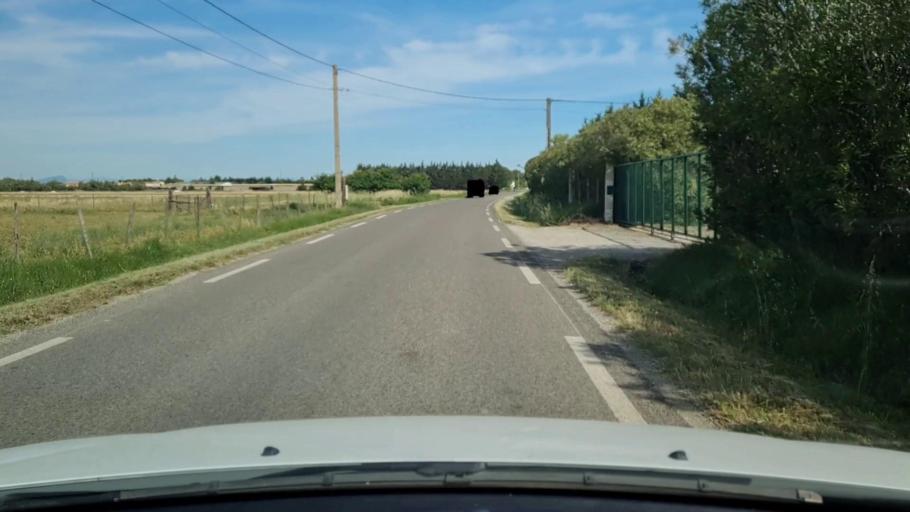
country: FR
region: Languedoc-Roussillon
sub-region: Departement de l'Herault
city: Marsillargues
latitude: 43.6236
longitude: 4.2005
